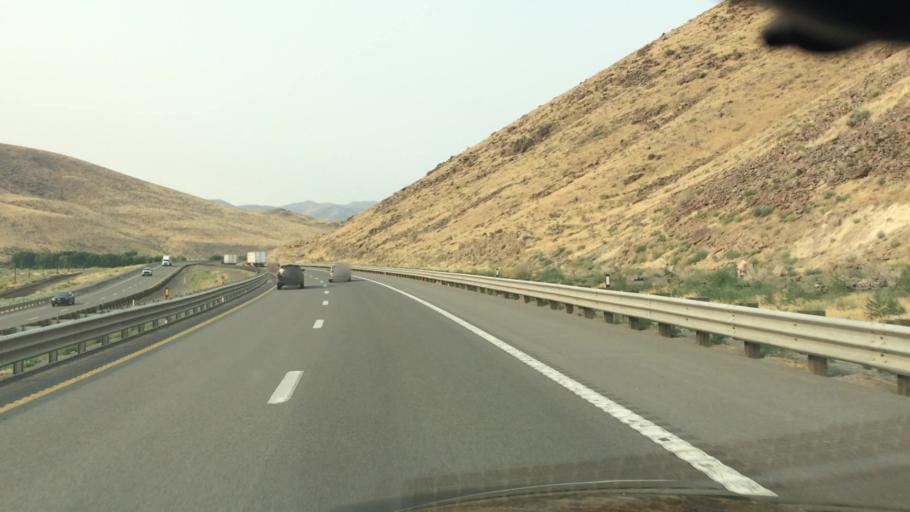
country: US
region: Nevada
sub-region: Lyon County
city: Fernley
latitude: 39.5763
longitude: -119.4725
